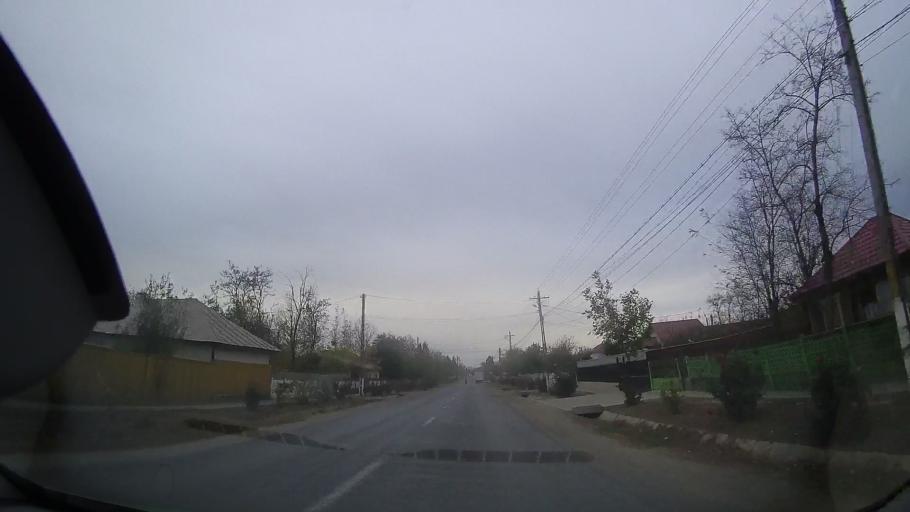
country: RO
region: Ialomita
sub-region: Comuna Grivita
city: Grivita
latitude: 44.7328
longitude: 27.2977
